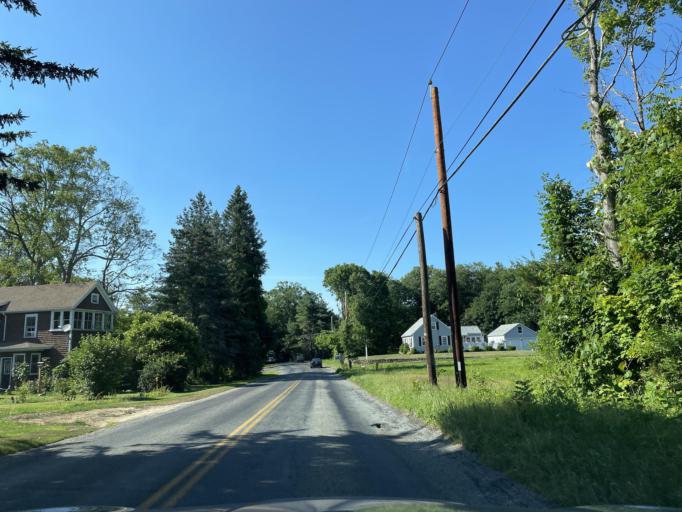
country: US
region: Massachusetts
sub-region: Worcester County
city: East Brookfield
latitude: 42.1699
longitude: -72.0292
